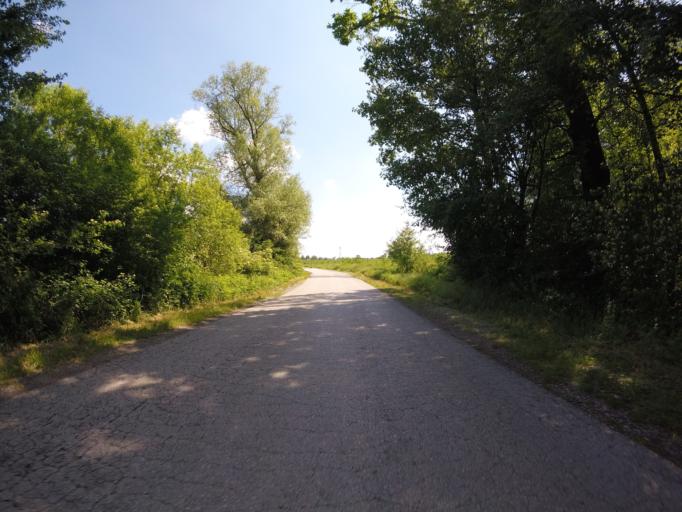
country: HR
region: Zagrebacka
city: Kuce
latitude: 45.6719
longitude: 16.1731
